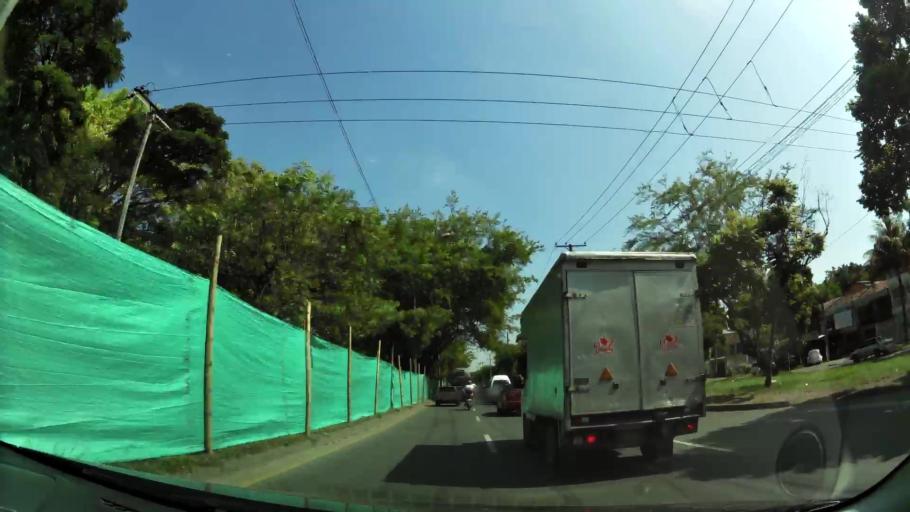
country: CO
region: Valle del Cauca
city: Cali
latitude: 3.3965
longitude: -76.5234
